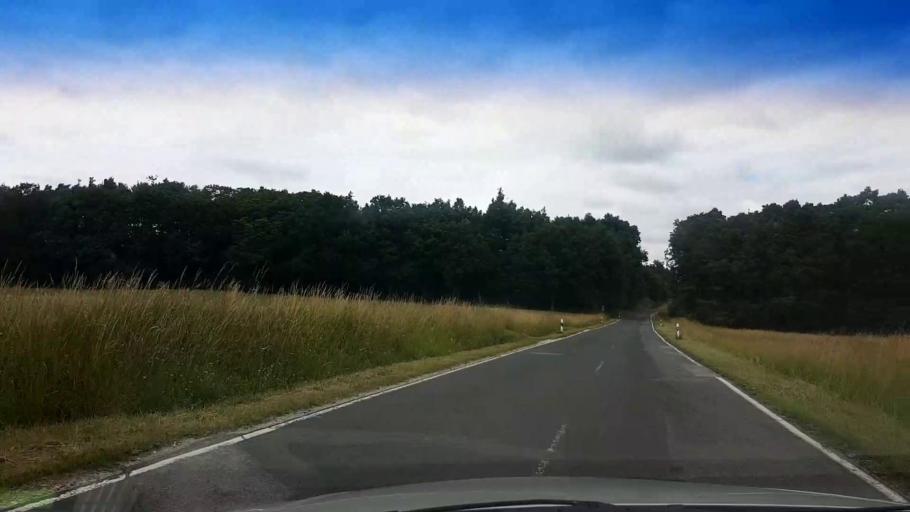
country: DE
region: Bavaria
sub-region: Upper Franconia
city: Oberhaid
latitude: 49.9383
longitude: 10.8167
